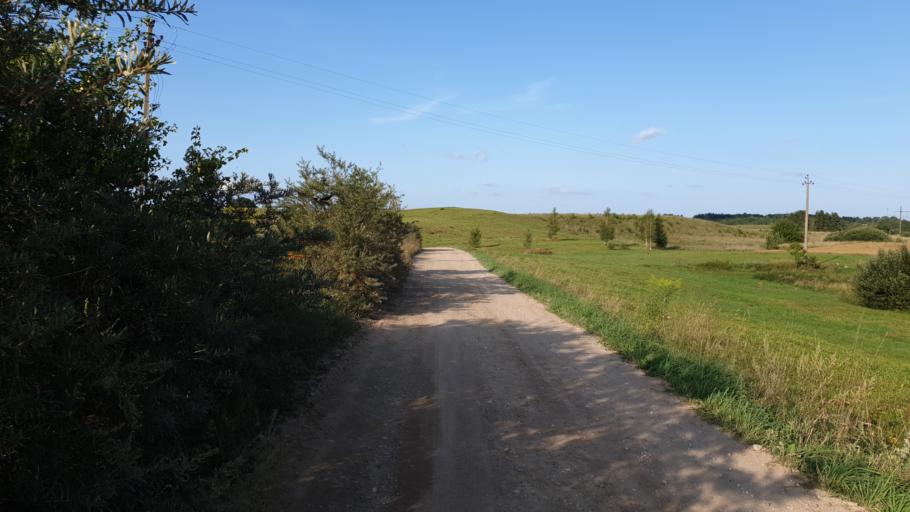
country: LT
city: Grigiskes
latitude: 54.7698
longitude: 25.0291
